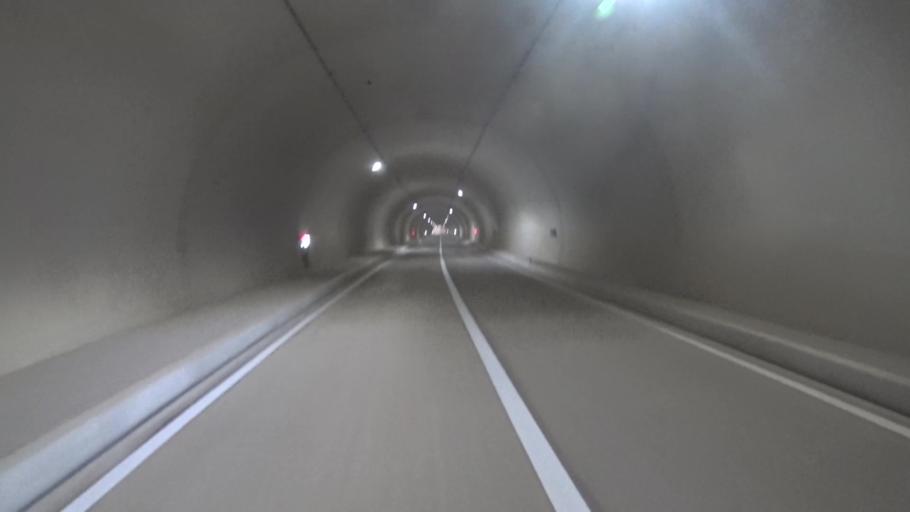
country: JP
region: Kyoto
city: Miyazu
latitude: 35.7436
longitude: 135.2561
